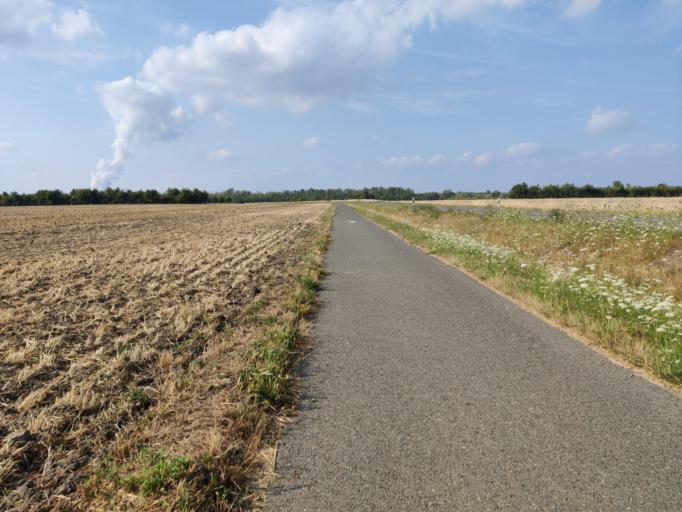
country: DE
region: Saxony
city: Lobstadt
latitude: 51.1250
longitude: 12.4232
